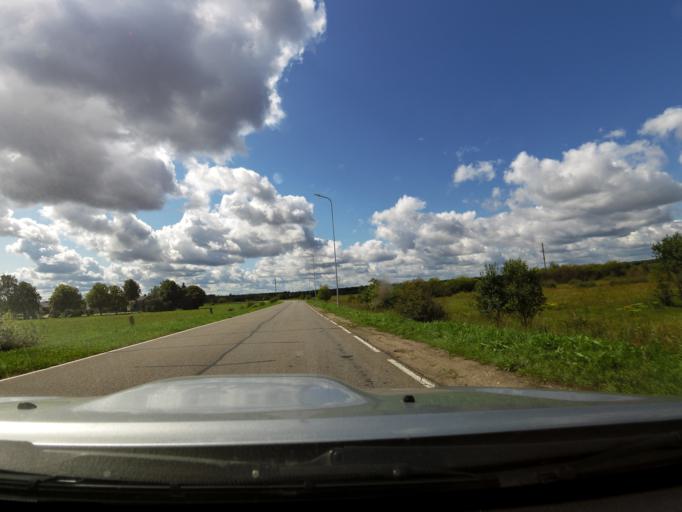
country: LV
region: Daugavpils
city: Daugavpils
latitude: 55.8744
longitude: 26.4947
